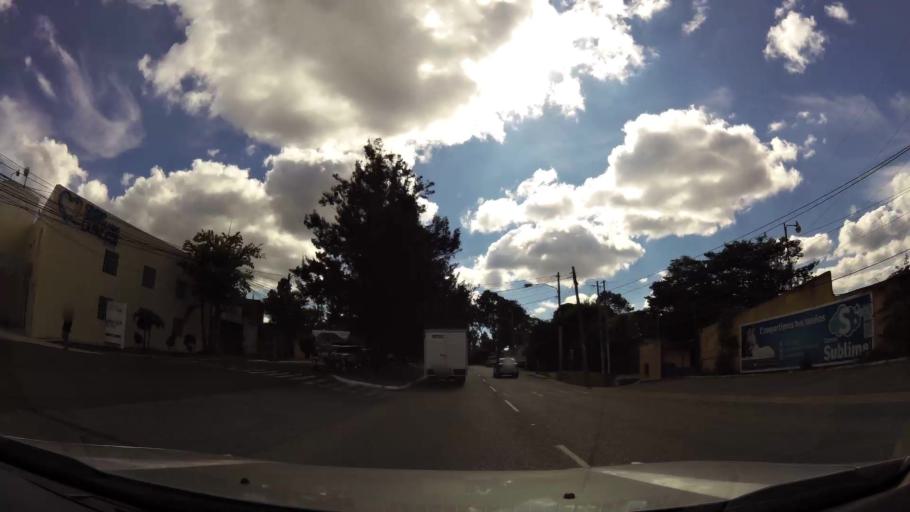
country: GT
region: Guatemala
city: Mixco
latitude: 14.6020
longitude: -90.5629
